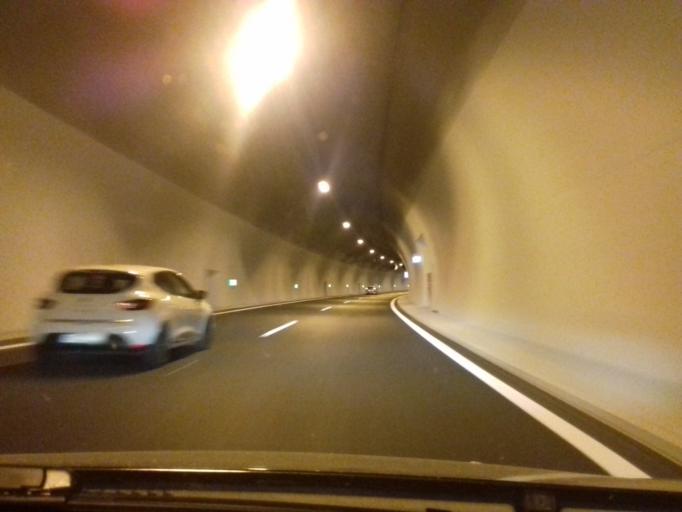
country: GR
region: West Greece
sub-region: Nomos Achaias
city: Akrata
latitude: 38.1681
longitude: 22.2674
